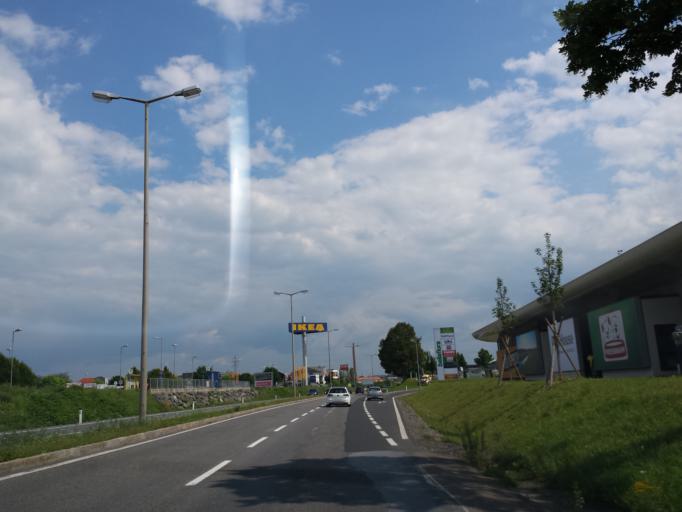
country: AT
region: Styria
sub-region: Graz Stadt
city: Wetzelsdorf
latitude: 47.0323
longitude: 15.4207
